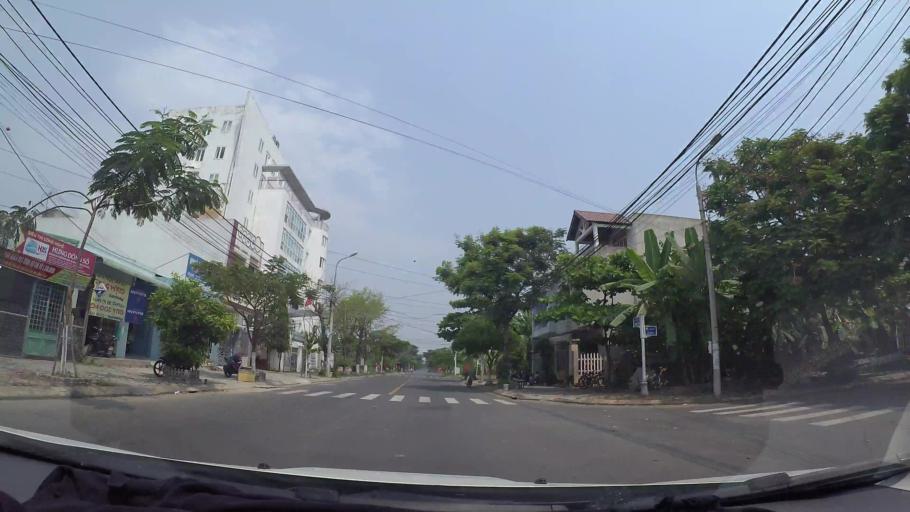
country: VN
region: Da Nang
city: Cam Le
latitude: 16.0002
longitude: 108.2105
